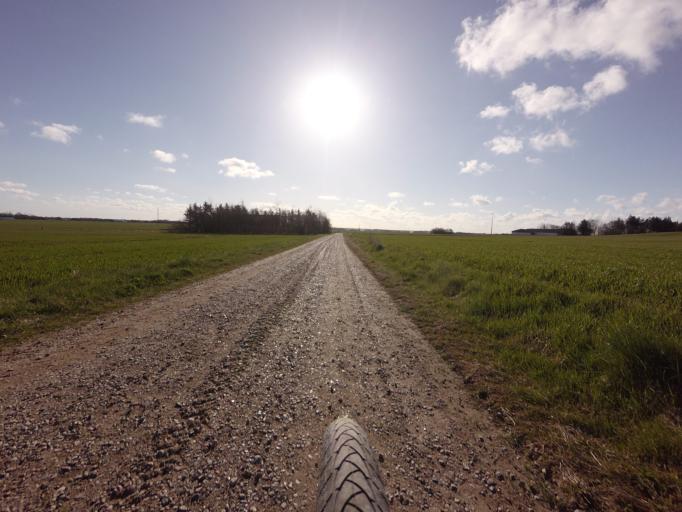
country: DK
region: North Denmark
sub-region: Hjorring Kommune
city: Vra
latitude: 57.3669
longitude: 9.8144
